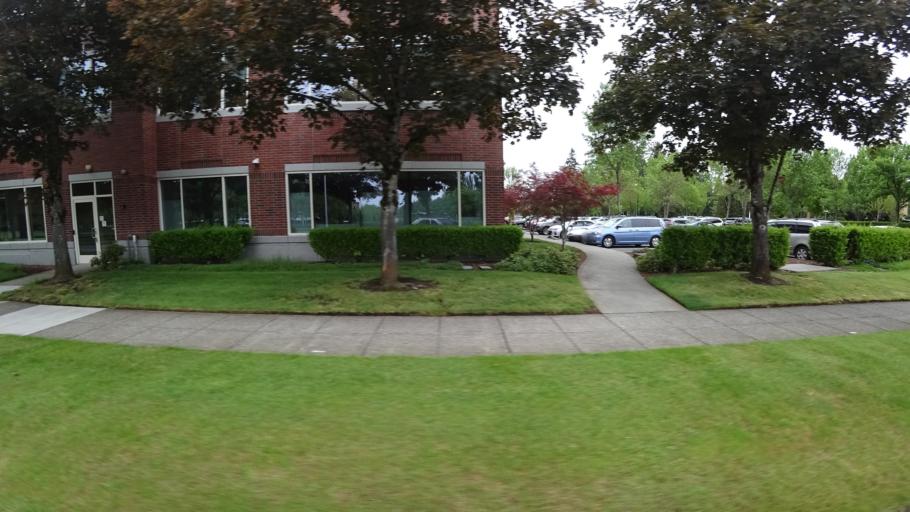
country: US
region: Oregon
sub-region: Washington County
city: Rockcreek
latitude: 45.5418
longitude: -122.8735
